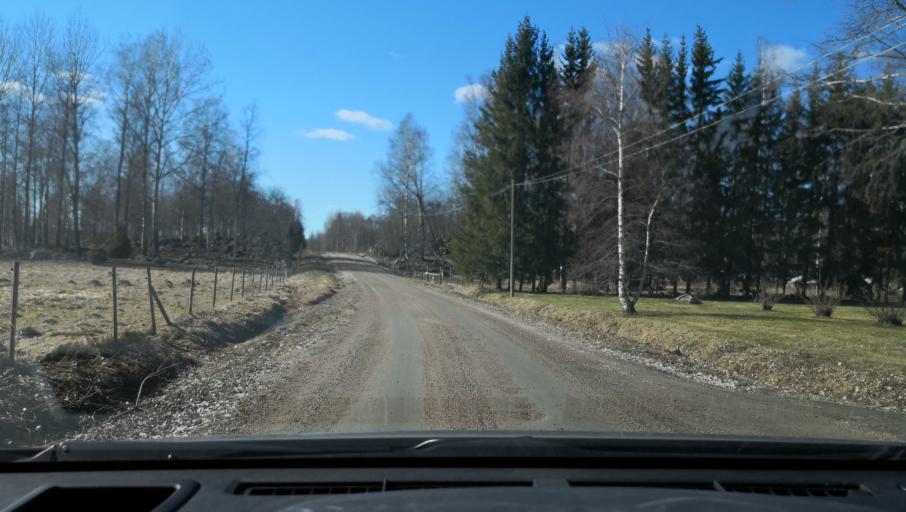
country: SE
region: Vaestmanland
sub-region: Sala Kommun
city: Sala
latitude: 60.1121
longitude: 16.6876
